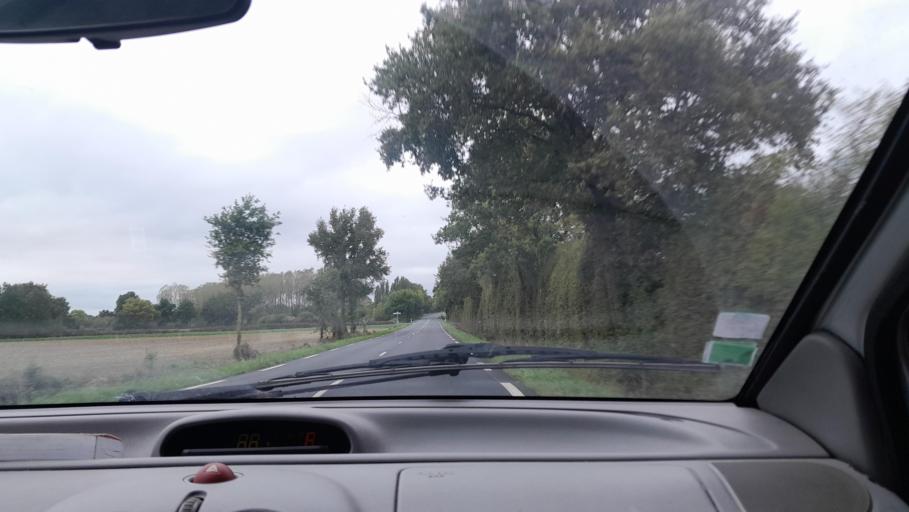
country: FR
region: Pays de la Loire
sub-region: Departement de la Loire-Atlantique
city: Saint-Mars-la-Jaille
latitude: 47.5853
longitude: -1.1937
